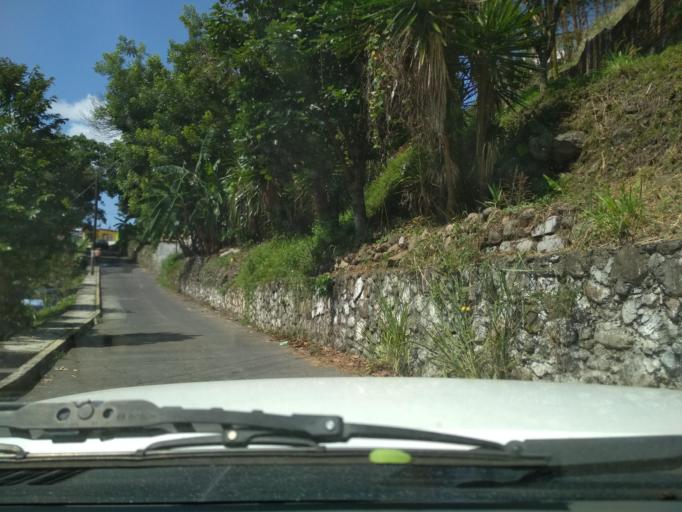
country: MX
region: Veracruz
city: Cordoba
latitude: 18.8797
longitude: -96.9129
